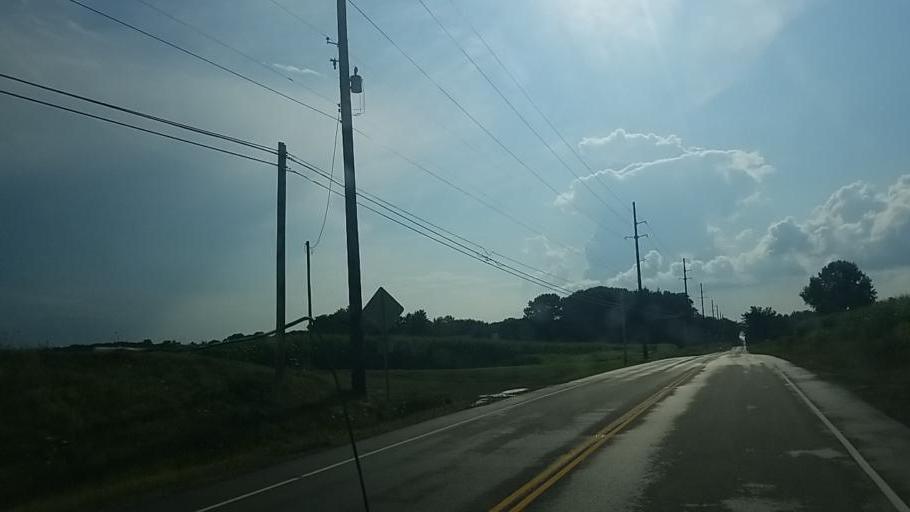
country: US
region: Ohio
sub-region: Wayne County
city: Wooster
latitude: 40.8580
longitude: -81.9544
